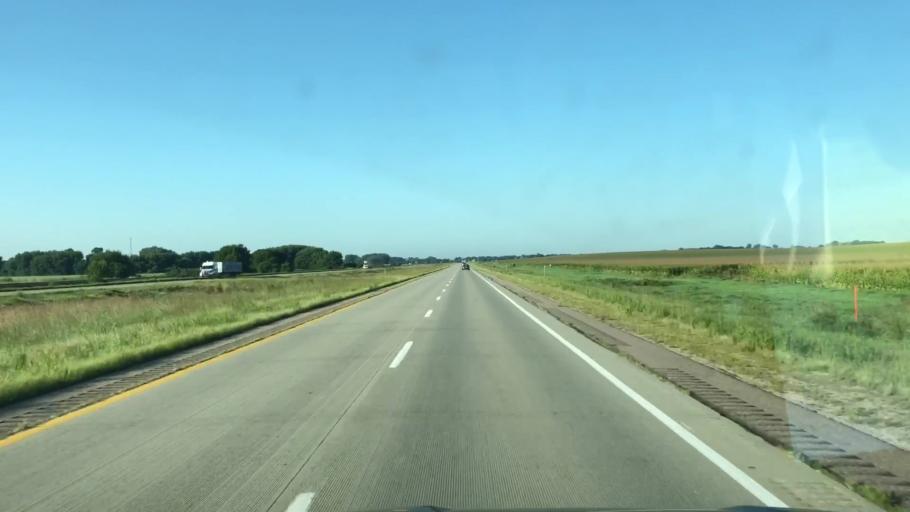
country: US
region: Iowa
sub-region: Plymouth County
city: Le Mars
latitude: 42.8769
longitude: -96.1050
